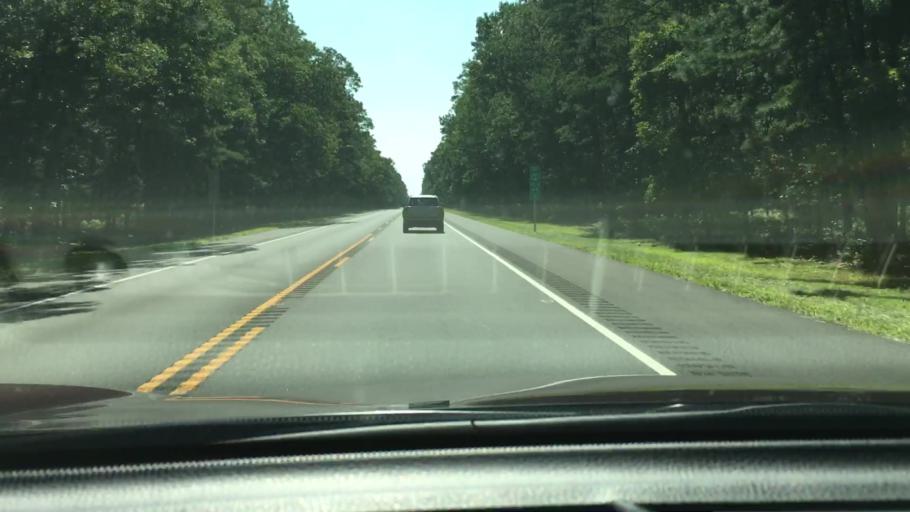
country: US
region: New Jersey
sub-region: Cumberland County
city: Laurel Lake
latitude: 39.3470
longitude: -74.9032
